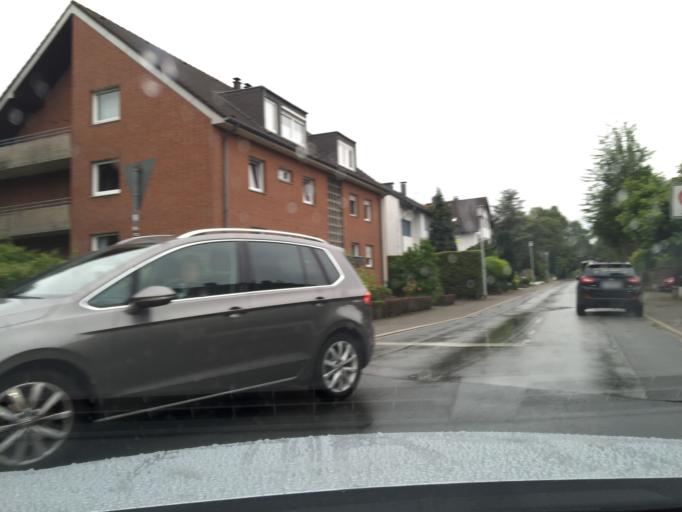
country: DE
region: North Rhine-Westphalia
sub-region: Regierungsbezirk Dusseldorf
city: Ratingen
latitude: 51.3370
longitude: 6.8997
